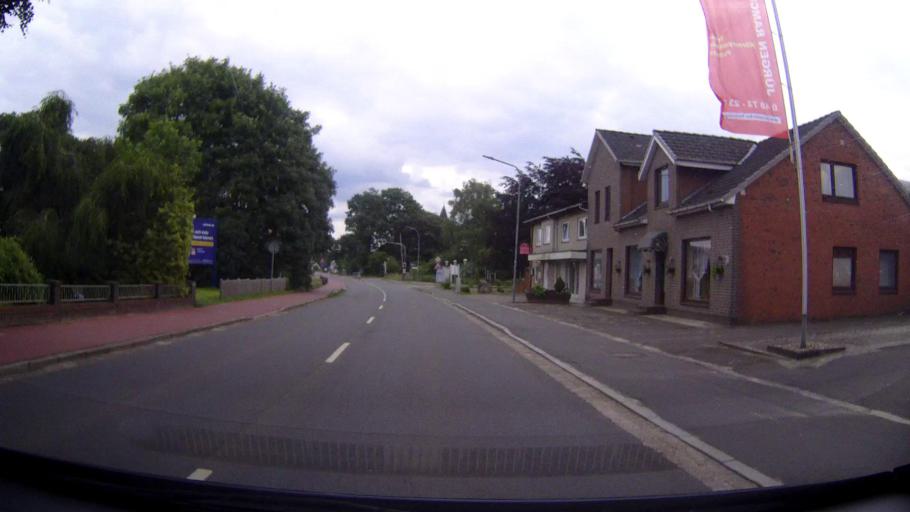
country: DE
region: Schleswig-Holstein
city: Hanerau-Hademarschen
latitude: 54.1232
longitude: 9.4232
